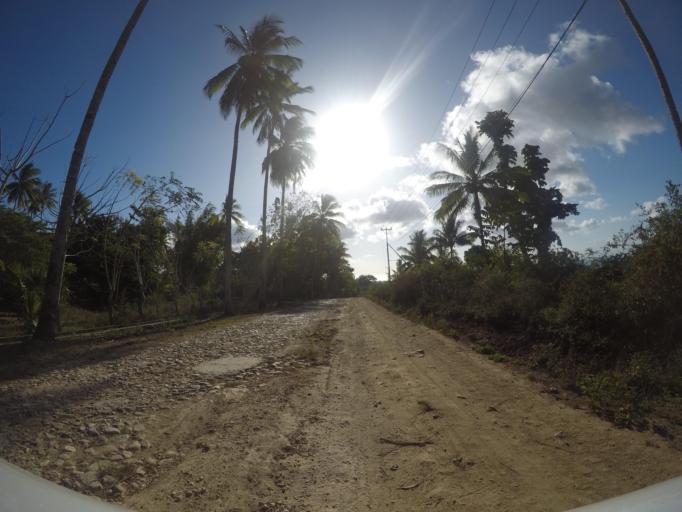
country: TL
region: Lautem
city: Lospalos
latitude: -8.4436
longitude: 126.8669
